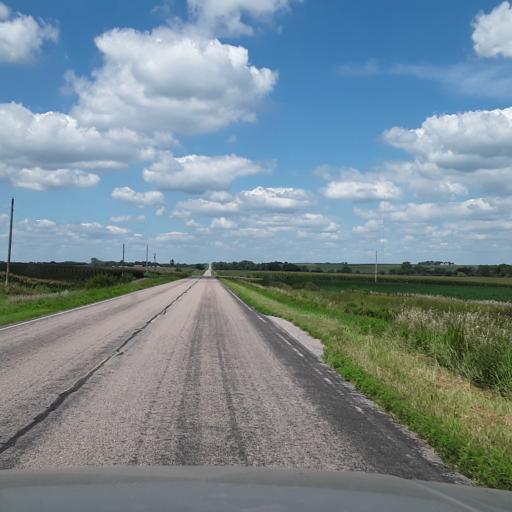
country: US
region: Nebraska
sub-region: Nance County
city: Genoa
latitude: 41.4887
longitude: -97.6956
